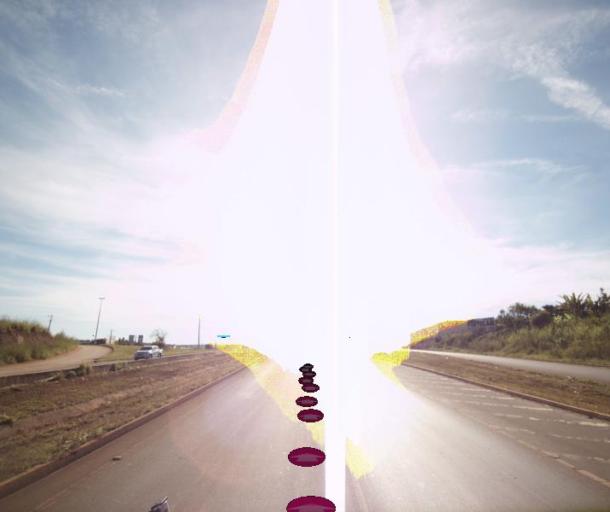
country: BR
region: Federal District
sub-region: Brasilia
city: Brasilia
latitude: -15.7552
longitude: -48.3298
